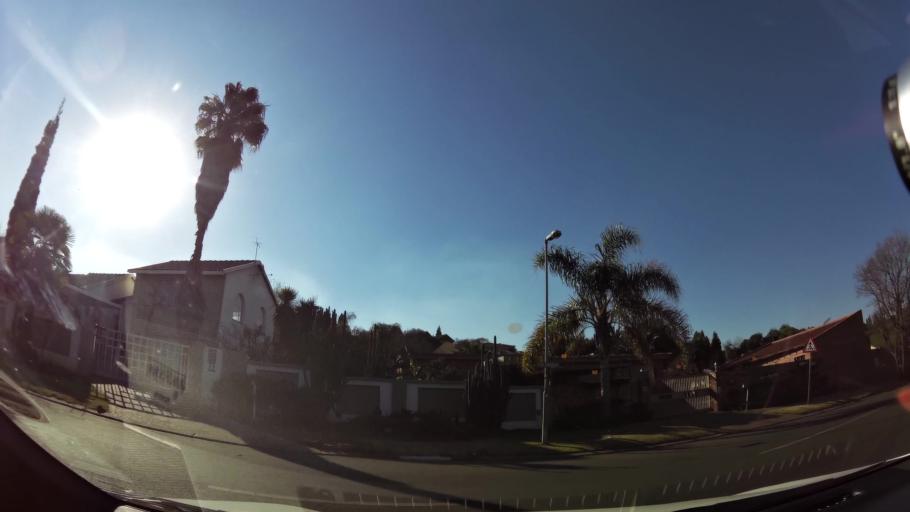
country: ZA
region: Gauteng
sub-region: City of Johannesburg Metropolitan Municipality
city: Johannesburg
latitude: -26.2905
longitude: 28.0510
